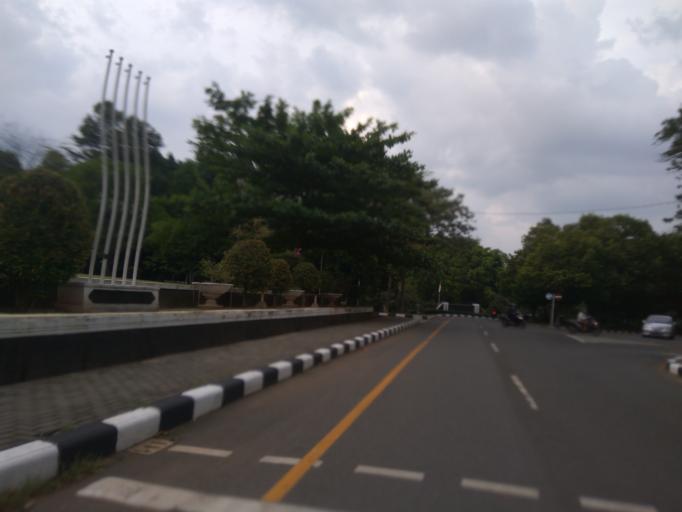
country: ID
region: Central Java
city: Semarang
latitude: -7.0497
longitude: 110.4388
